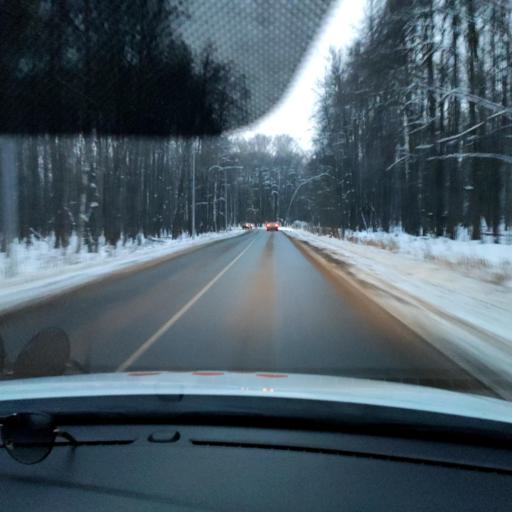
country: RU
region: Tatarstan
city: Vysokaya Gora
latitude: 55.9289
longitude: 49.1937
